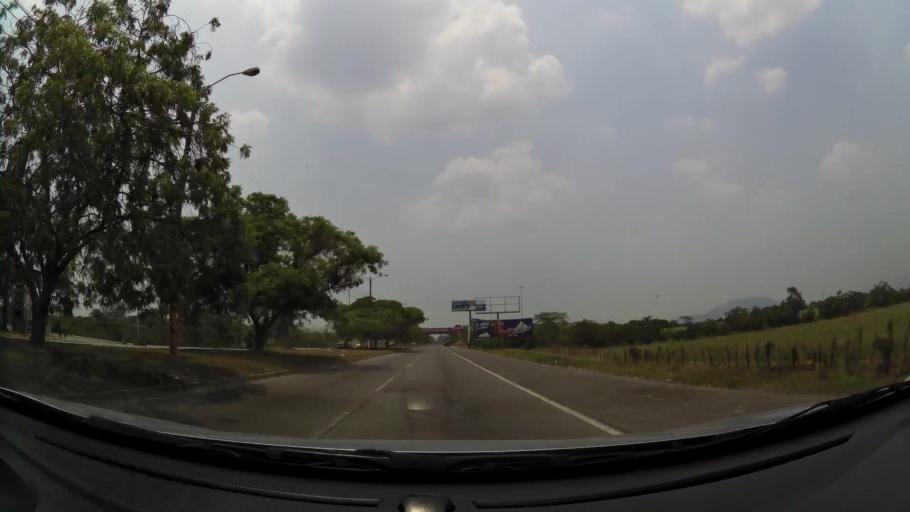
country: HN
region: Cortes
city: La Lima
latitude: 15.4467
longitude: -87.9435
